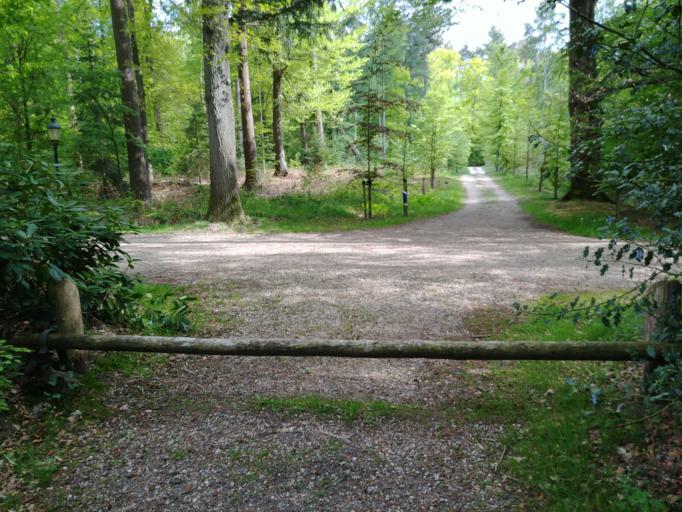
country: NL
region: Gelderland
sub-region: Gemeente Apeldoorn
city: Uddel
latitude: 52.2880
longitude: 5.7365
